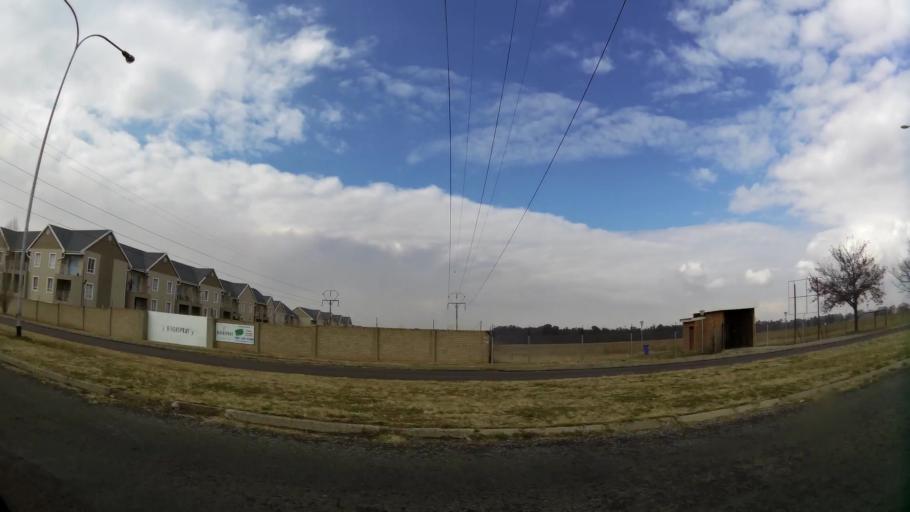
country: ZA
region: Gauteng
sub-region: Sedibeng District Municipality
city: Vanderbijlpark
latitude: -26.7192
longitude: 27.8843
